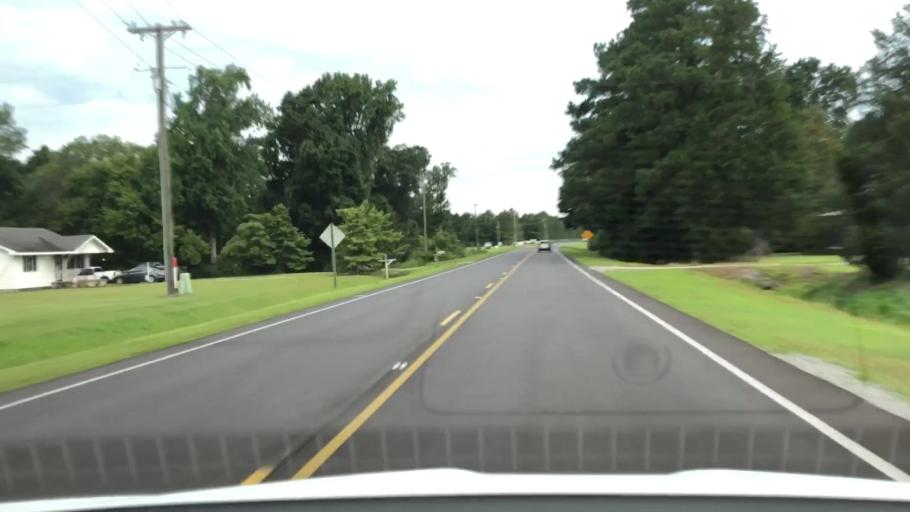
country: US
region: North Carolina
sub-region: Jones County
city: Maysville
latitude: 34.8813
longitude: -77.2074
